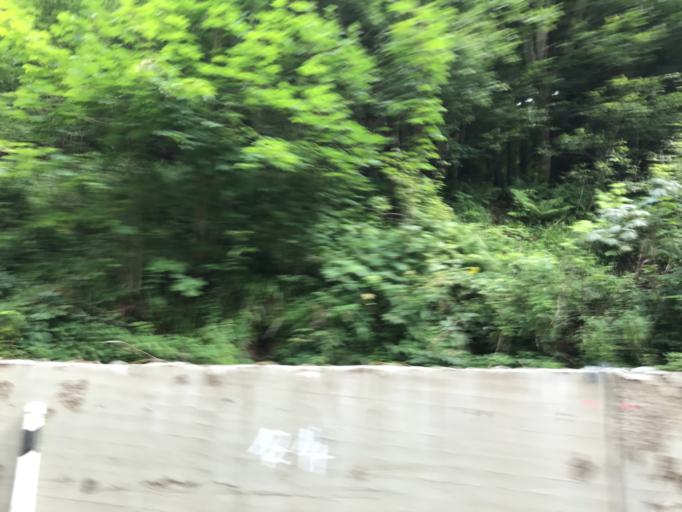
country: DE
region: Lower Saxony
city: Bad Harzburg
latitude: 51.8500
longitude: 10.5454
